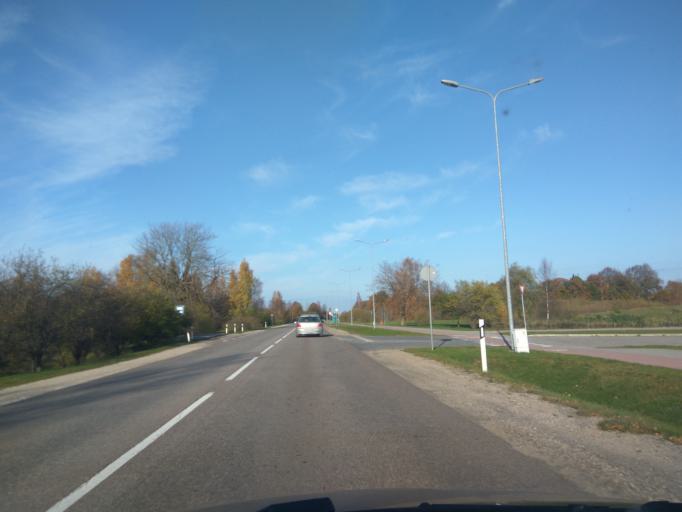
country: LV
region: Ventspils
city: Ventspils
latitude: 57.3591
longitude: 21.5633
